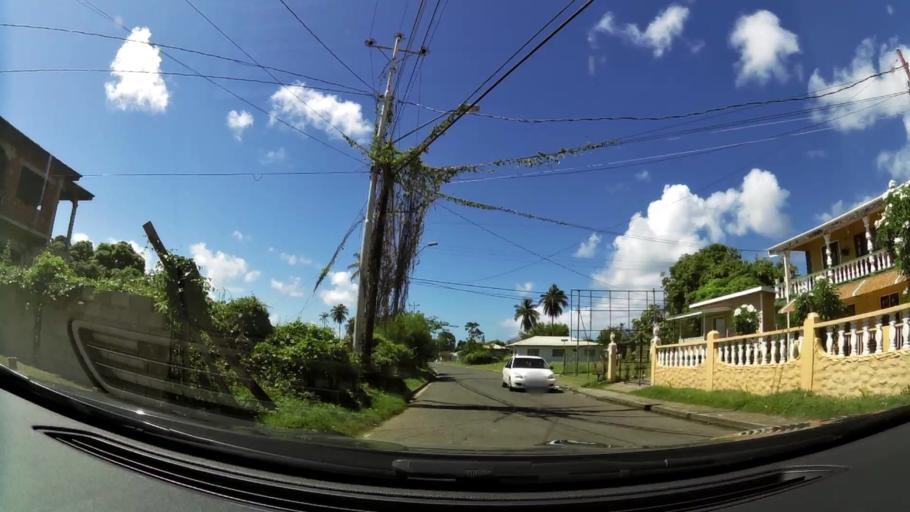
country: TT
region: Tobago
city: Scarborough
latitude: 11.1824
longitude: -60.8040
